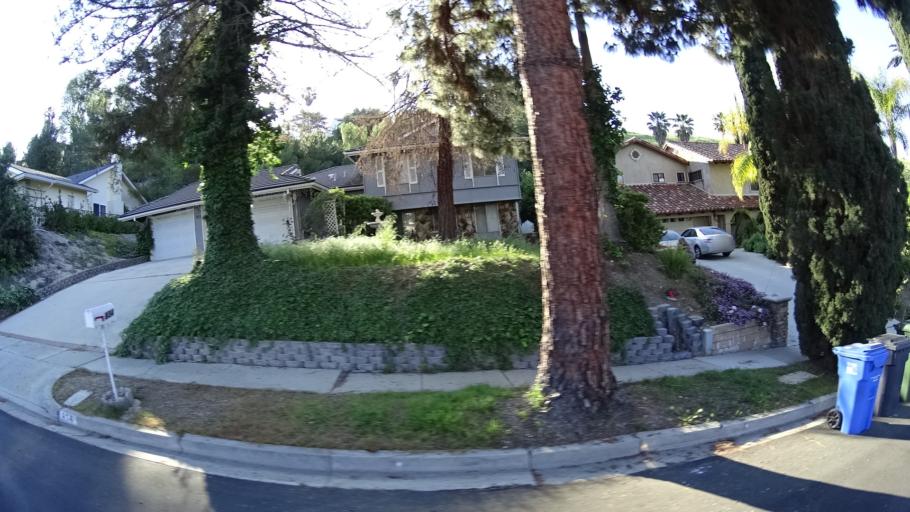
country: US
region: California
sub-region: Ventura County
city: Thousand Oaks
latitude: 34.1881
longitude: -118.8445
